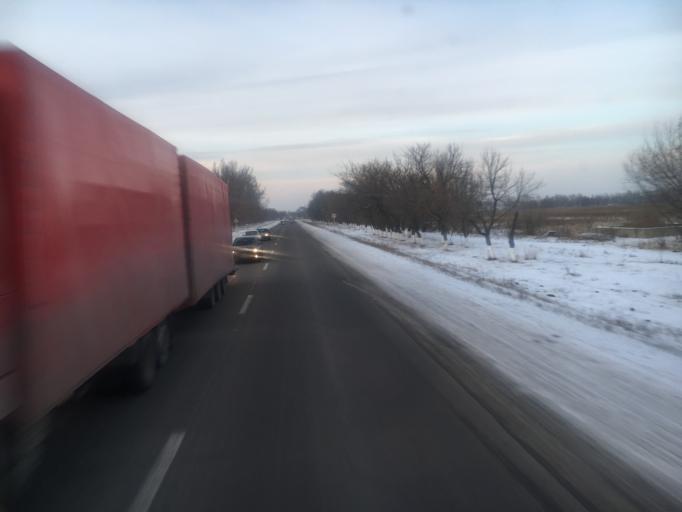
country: KZ
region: Almaty Oblysy
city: Burunday
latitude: 43.3592
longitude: 76.6443
